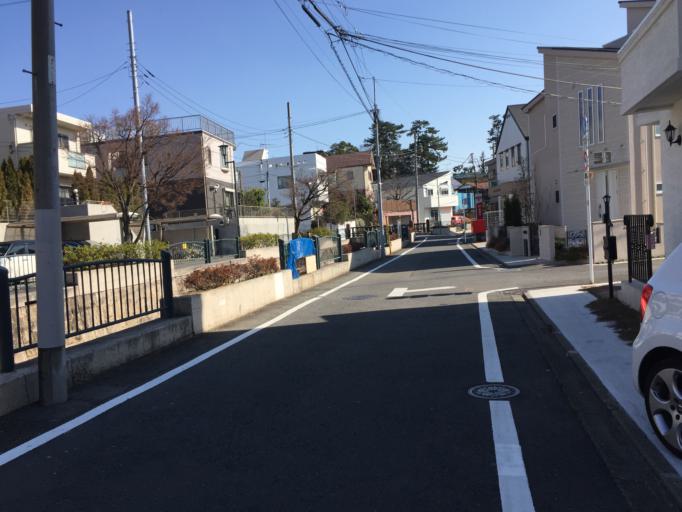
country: JP
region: Kanagawa
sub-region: Kawasaki-shi
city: Kawasaki
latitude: 35.5971
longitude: 139.6562
